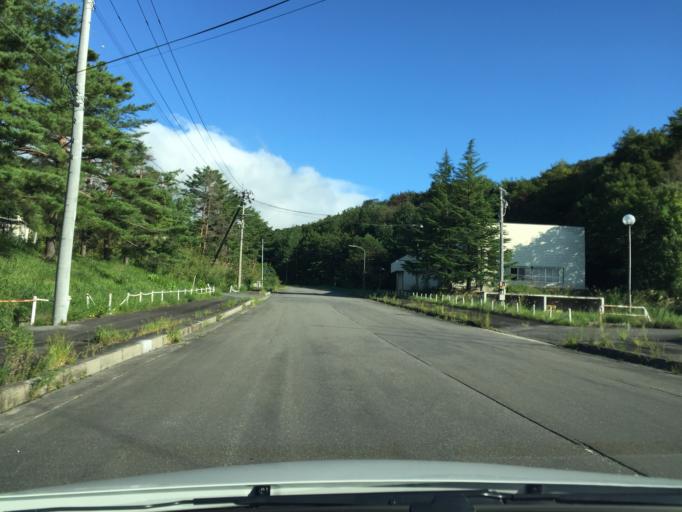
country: JP
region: Yamagata
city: Yonezawa
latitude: 37.9062
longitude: 140.1848
